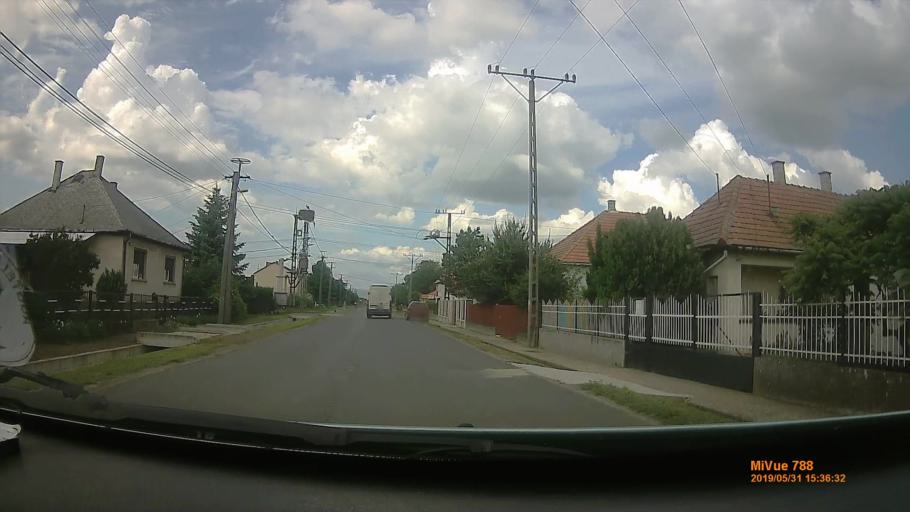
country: HU
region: Borsod-Abauj-Zemplen
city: Prugy
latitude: 48.0847
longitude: 21.2402
